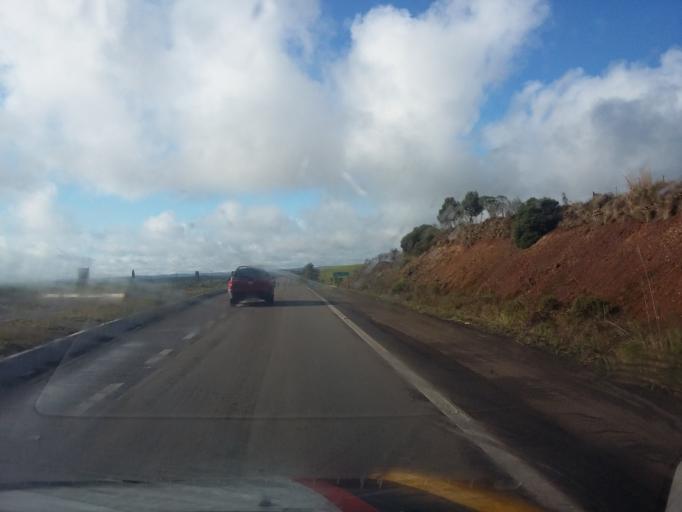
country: BR
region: Rio Grande do Sul
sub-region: Vacaria
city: Vacaria
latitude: -28.5341
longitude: -50.8001
